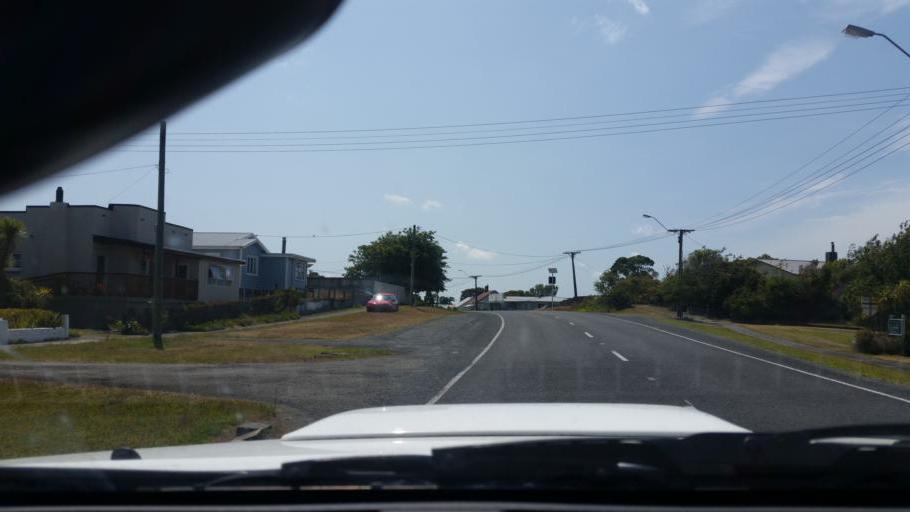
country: NZ
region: Northland
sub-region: Kaipara District
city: Dargaville
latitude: -36.0296
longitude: 173.9221
